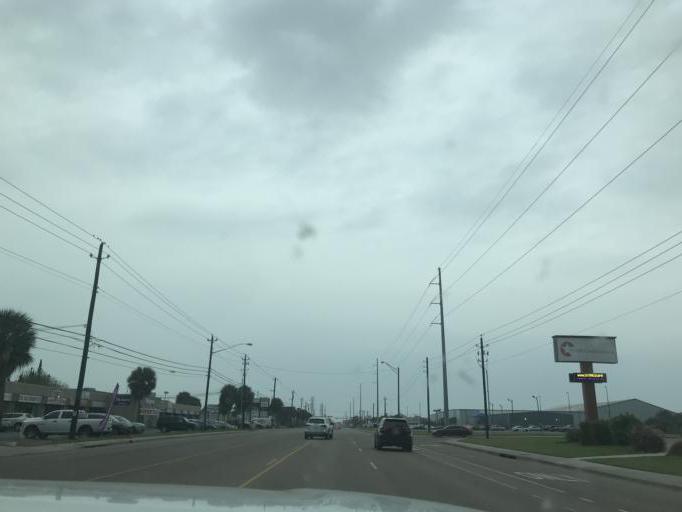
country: US
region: Texas
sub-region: Nueces County
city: Corpus Christi
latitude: 27.6938
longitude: -97.3669
